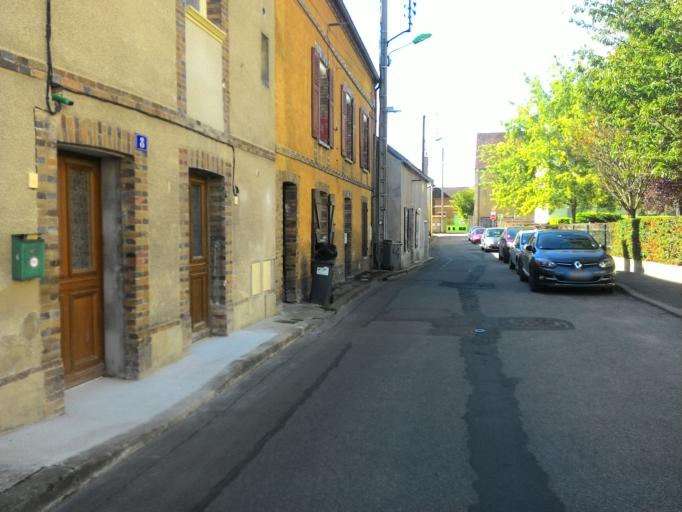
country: FR
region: Bourgogne
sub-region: Departement de l'Yonne
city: Sens
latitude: 48.1937
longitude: 3.2819
